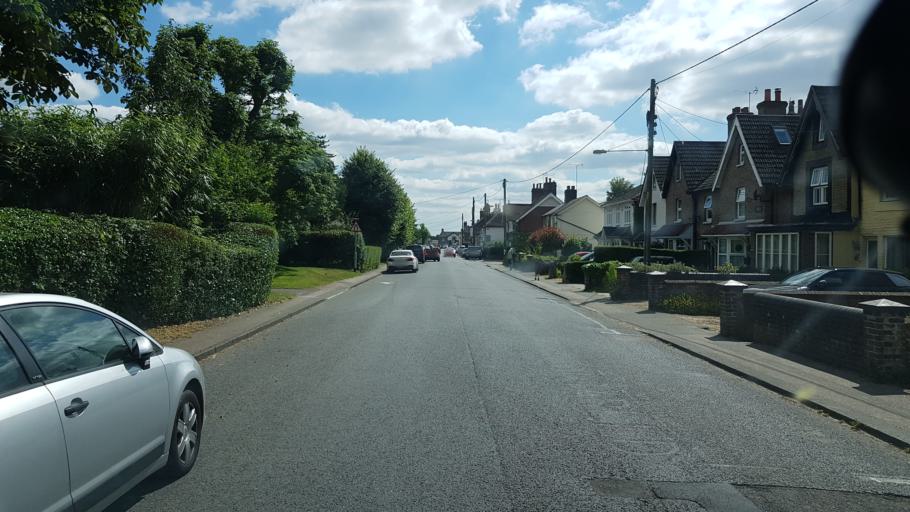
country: GB
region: England
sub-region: West Sussex
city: Broadfield
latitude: 51.0557
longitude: -0.1990
